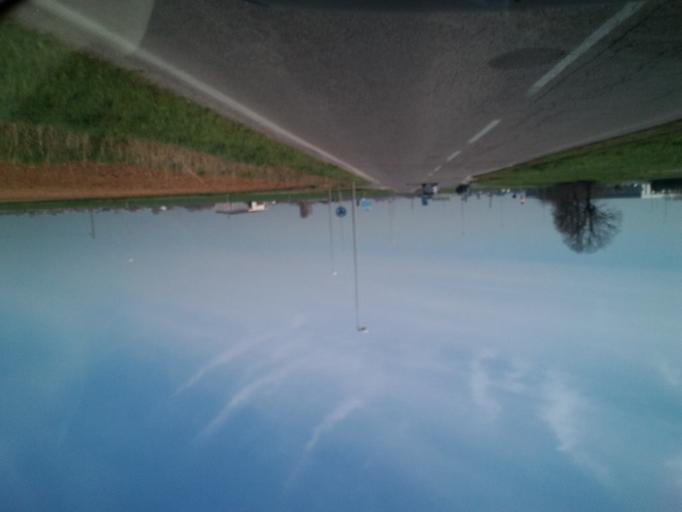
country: IT
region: Lombardy
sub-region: Provincia di Mantova
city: Malavicina
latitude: 45.2923
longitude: 10.8038
